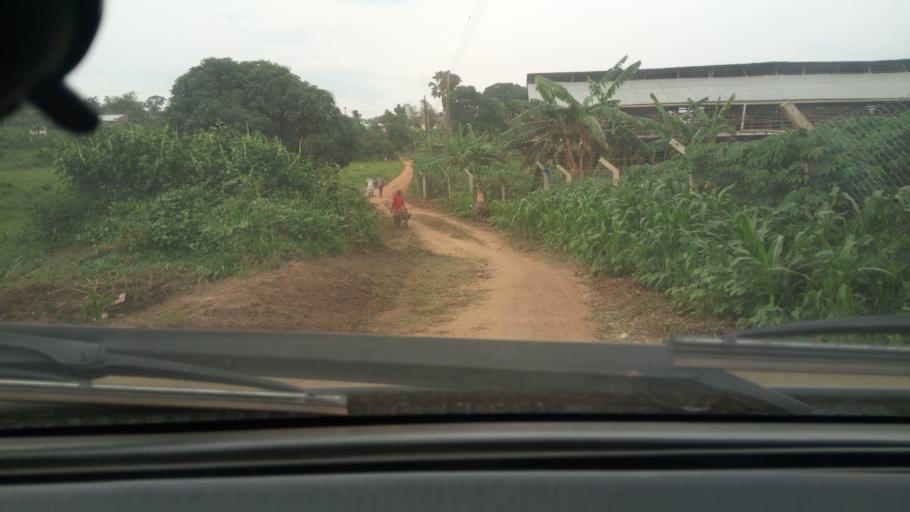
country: UG
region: Central Region
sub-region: Mityana District
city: Mityana
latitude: 0.5666
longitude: 32.1998
